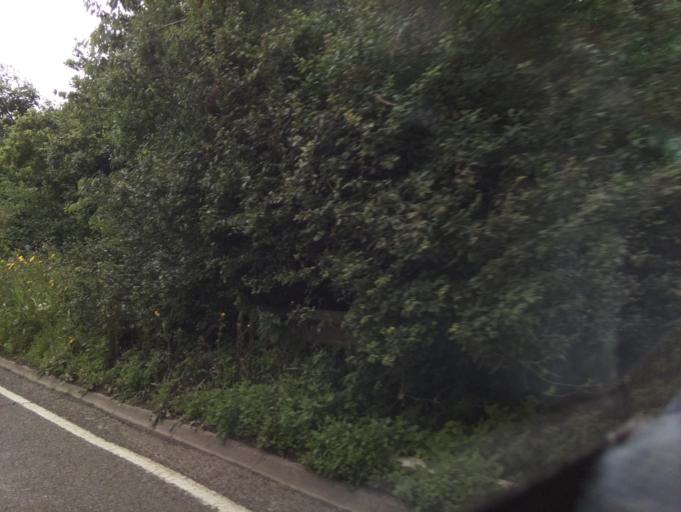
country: GB
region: England
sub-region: Northamptonshire
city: Geddington
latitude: 52.4468
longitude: -0.7351
